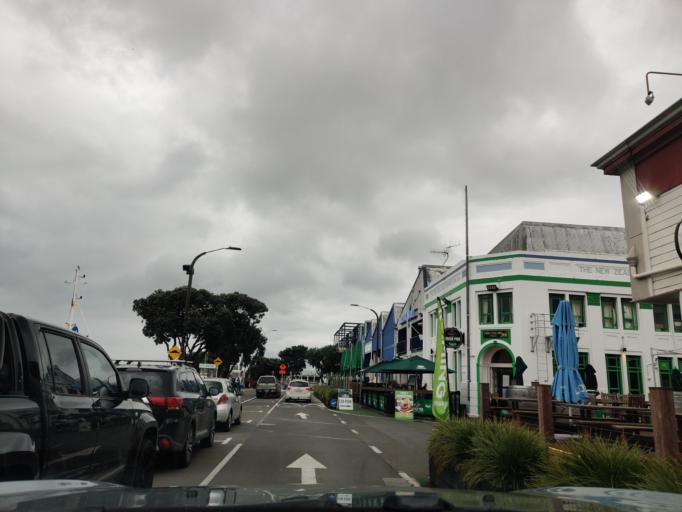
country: NZ
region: Hawke's Bay
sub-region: Napier City
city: Napier
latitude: -39.4831
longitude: 176.8942
